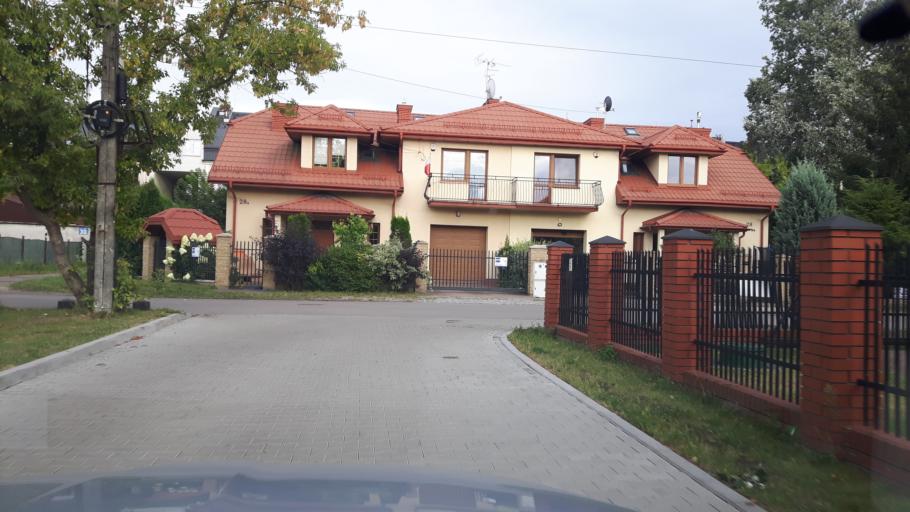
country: PL
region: Masovian Voivodeship
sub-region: Powiat wolominski
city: Marki
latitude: 52.3230
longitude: 21.1012
